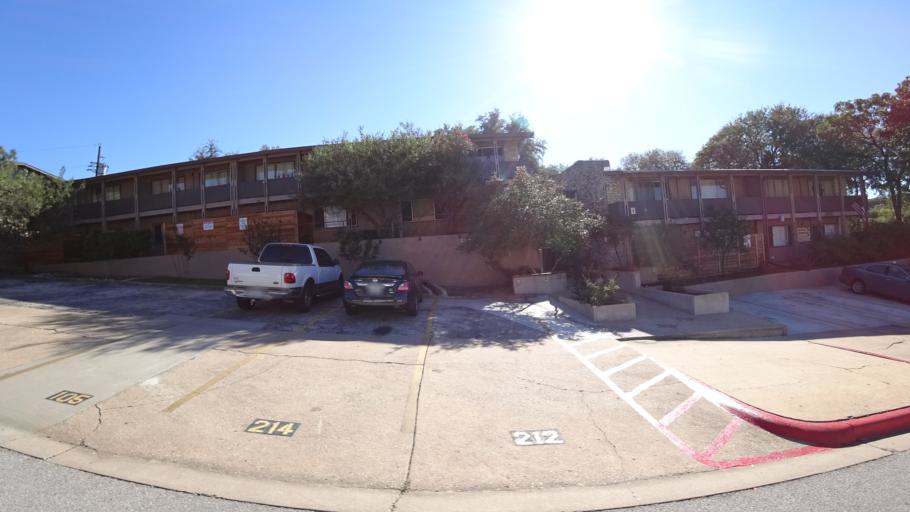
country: US
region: Texas
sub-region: Travis County
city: Austin
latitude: 30.2440
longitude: -97.7343
